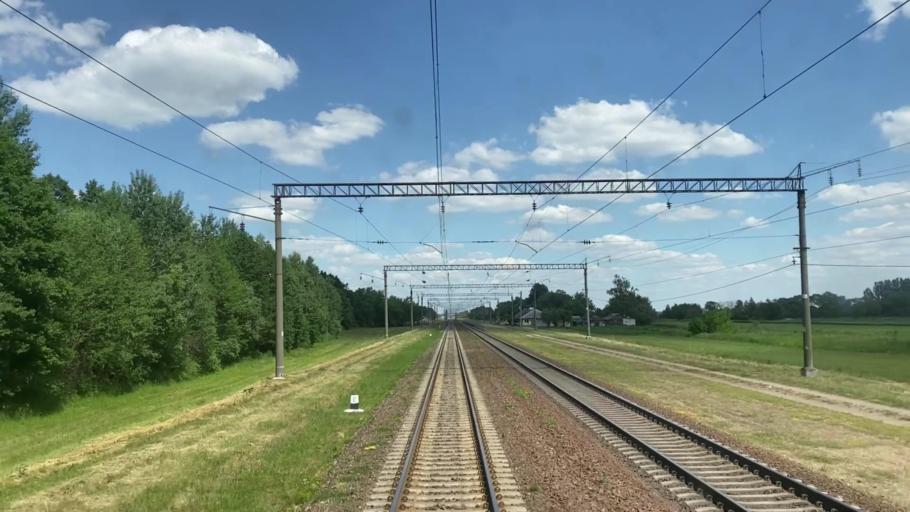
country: BY
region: Brest
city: Charnawchytsy
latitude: 52.1417
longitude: 23.8468
